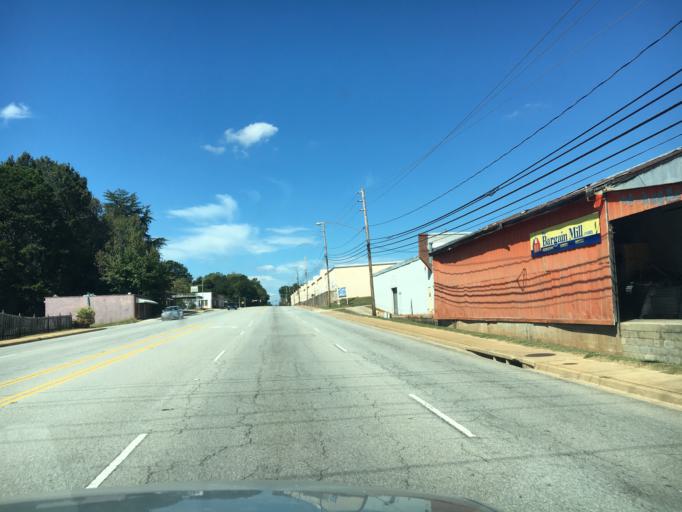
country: US
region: South Carolina
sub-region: Spartanburg County
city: Spartanburg
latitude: 34.9353
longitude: -81.9016
